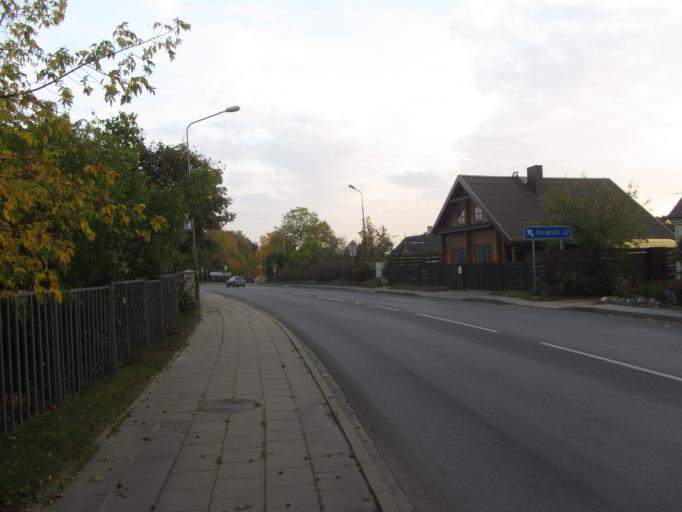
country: LT
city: Trakai
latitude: 54.6310
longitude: 24.9351
